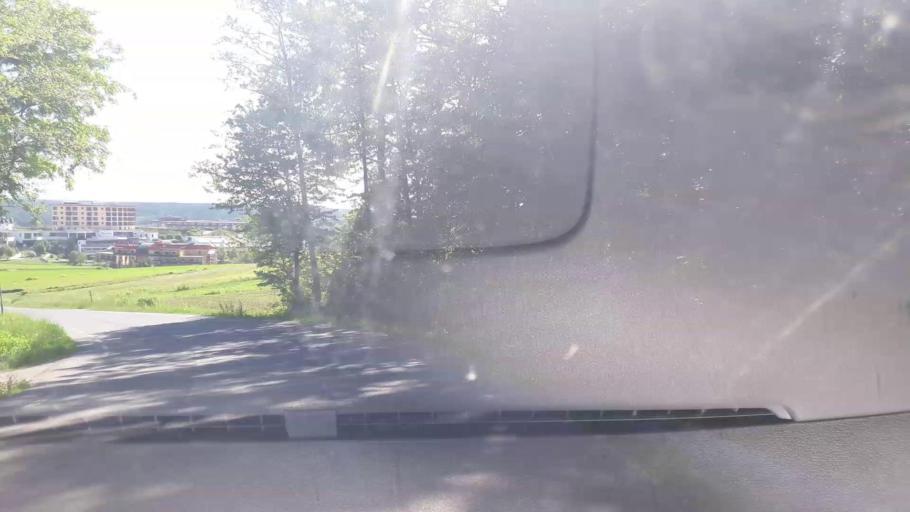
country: AT
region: Burgenland
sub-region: Politischer Bezirk Gussing
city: Stegersbach
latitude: 47.1706
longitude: 16.1430
